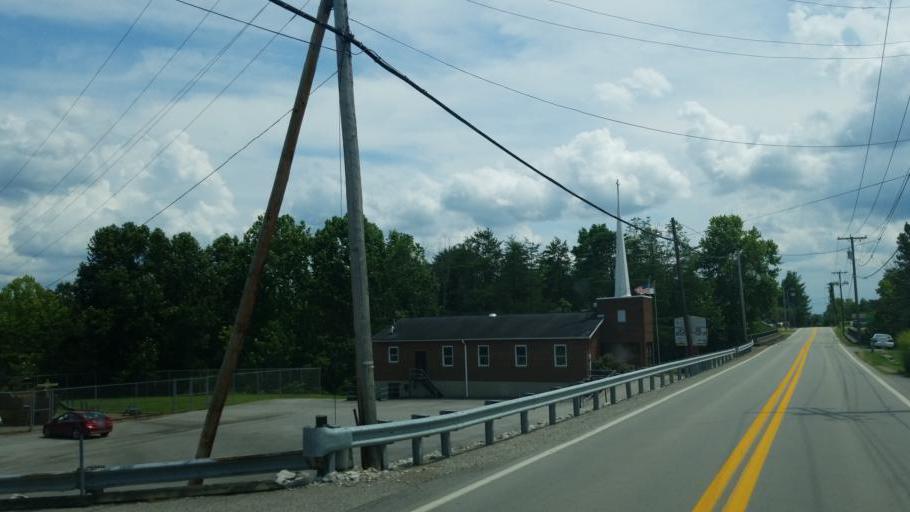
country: US
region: West Virginia
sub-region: Kanawha County
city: Nitro
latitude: 38.4403
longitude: -81.8557
